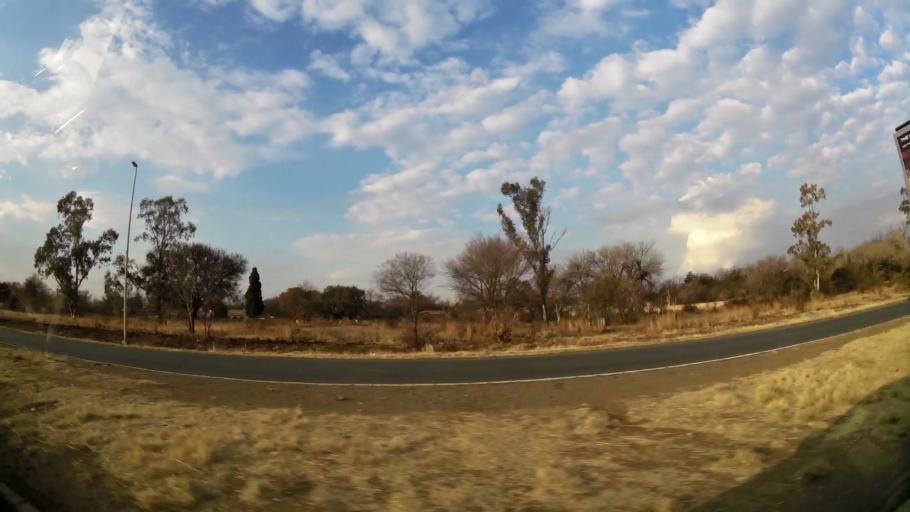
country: ZA
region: Gauteng
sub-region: Sedibeng District Municipality
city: Vanderbijlpark
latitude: -26.7062
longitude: 27.8136
